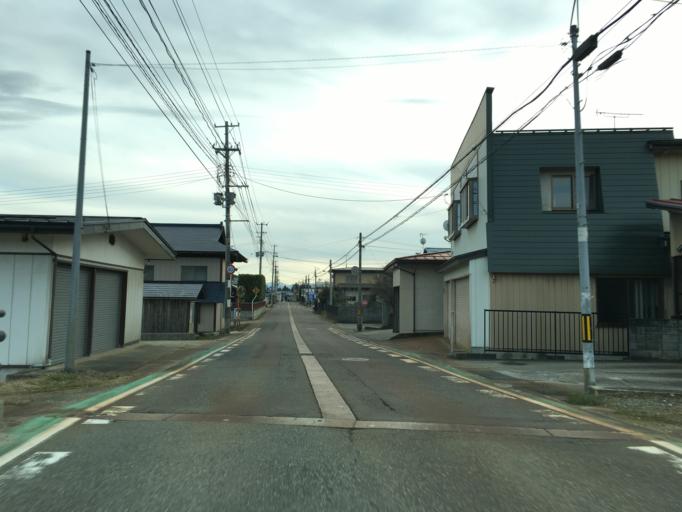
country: JP
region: Yamagata
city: Nagai
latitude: 38.1767
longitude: 140.0645
